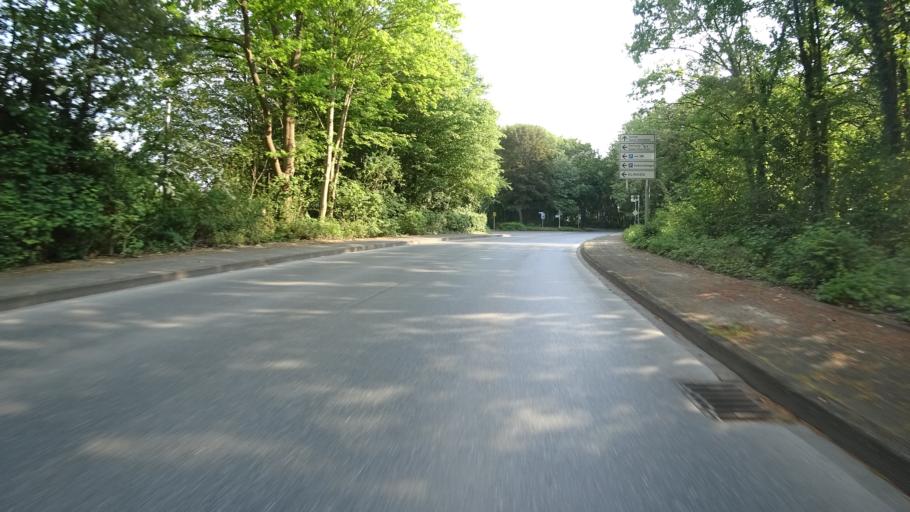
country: DE
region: North Rhine-Westphalia
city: Erwitte
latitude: 51.6320
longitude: 8.3510
